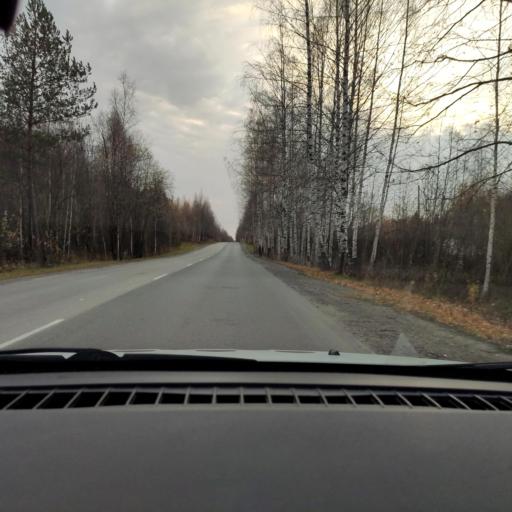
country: RU
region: Perm
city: Polazna
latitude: 58.1048
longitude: 56.4164
